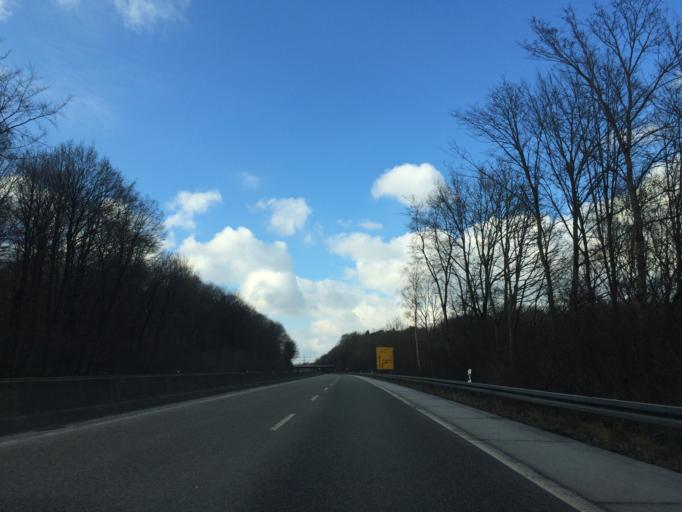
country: DE
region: Hesse
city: Kelkheim (Taunus)
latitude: 50.1470
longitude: 8.4720
